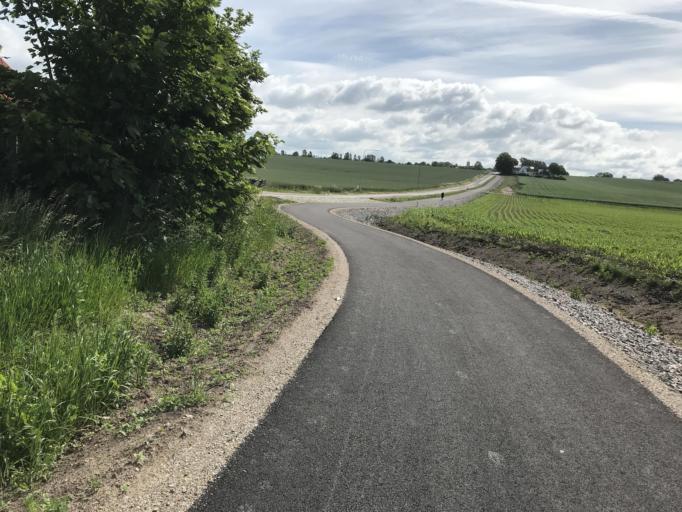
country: SE
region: Skane
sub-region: Helsingborg
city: Glumslov
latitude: 55.9424
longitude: 12.7900
